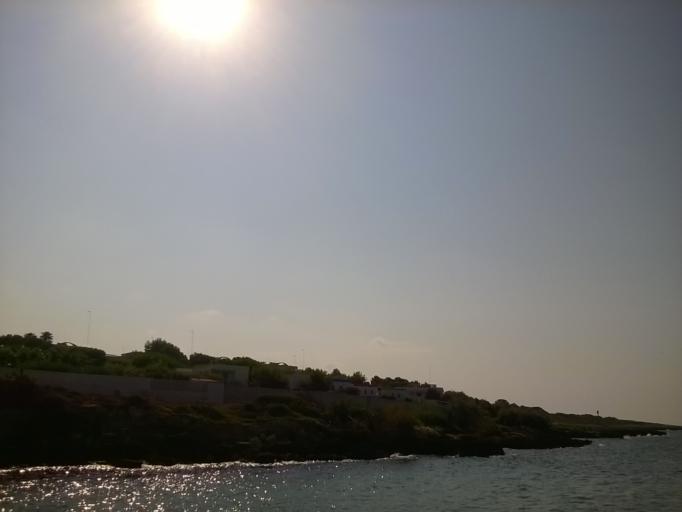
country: IT
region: Apulia
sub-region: Provincia di Taranto
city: Taranto
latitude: 40.3956
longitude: 17.2563
